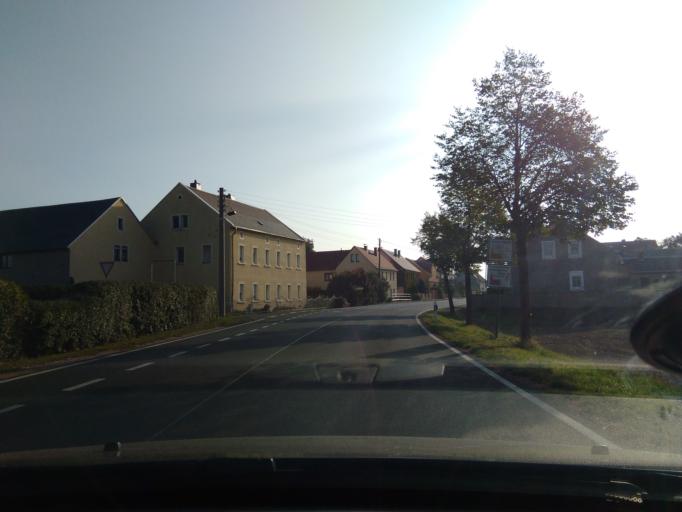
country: DE
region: Saxony
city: Niederau
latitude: 51.1343
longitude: 13.5368
